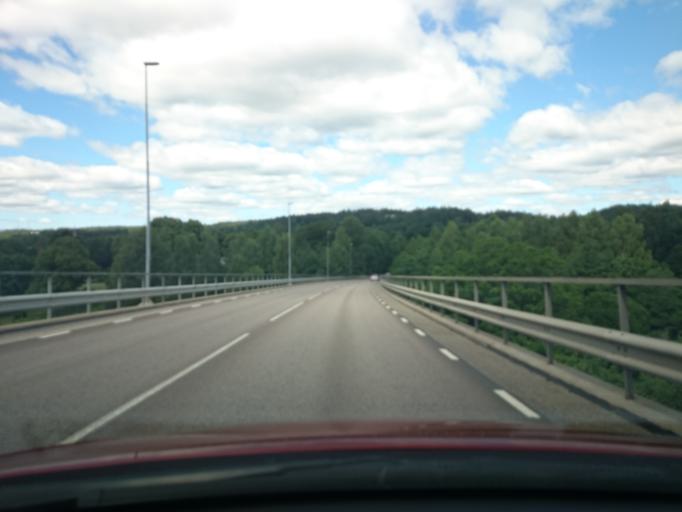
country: SE
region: Vaestra Goetaland
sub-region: Lerums Kommun
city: Lerum
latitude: 57.7751
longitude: 12.2894
